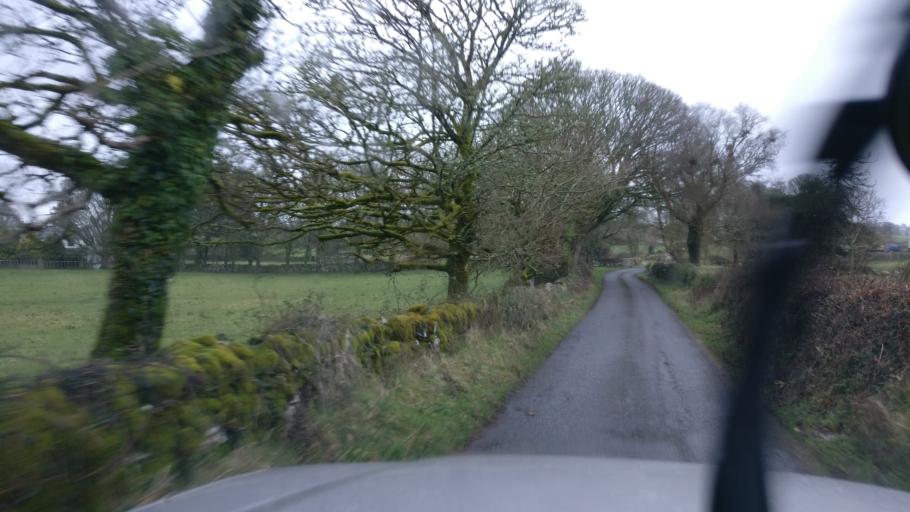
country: IE
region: Connaught
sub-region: County Galway
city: Loughrea
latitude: 53.1793
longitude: -8.6080
